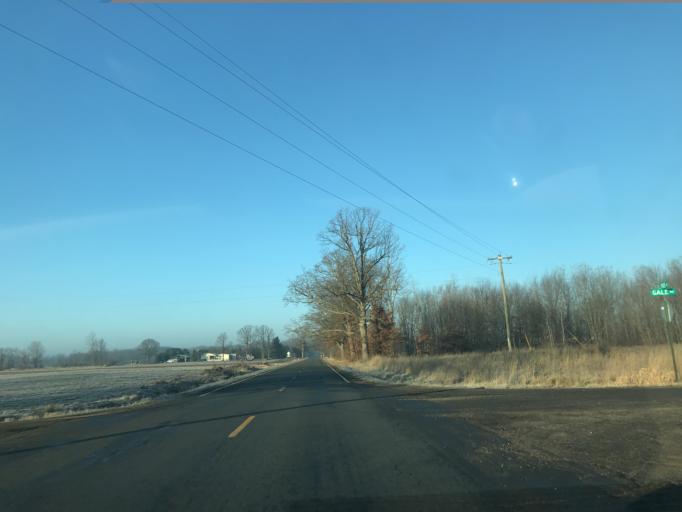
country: US
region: Michigan
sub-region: Eaton County
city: Eaton Rapids
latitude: 42.4511
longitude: -84.5798
